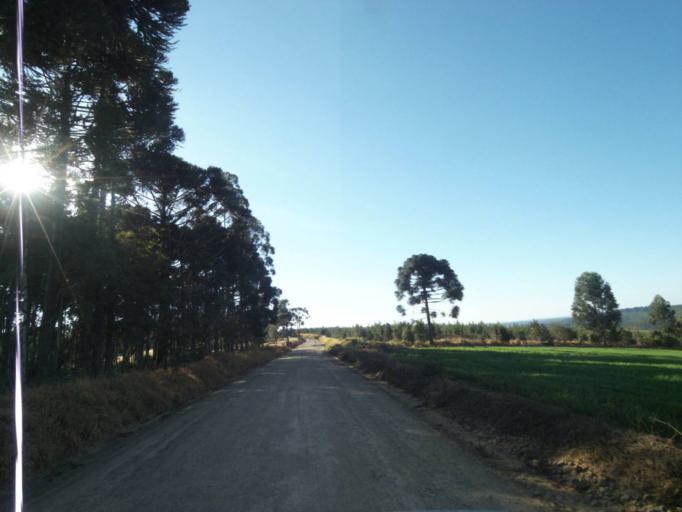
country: BR
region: Parana
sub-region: Telemaco Borba
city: Telemaco Borba
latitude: -24.5173
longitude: -50.6474
